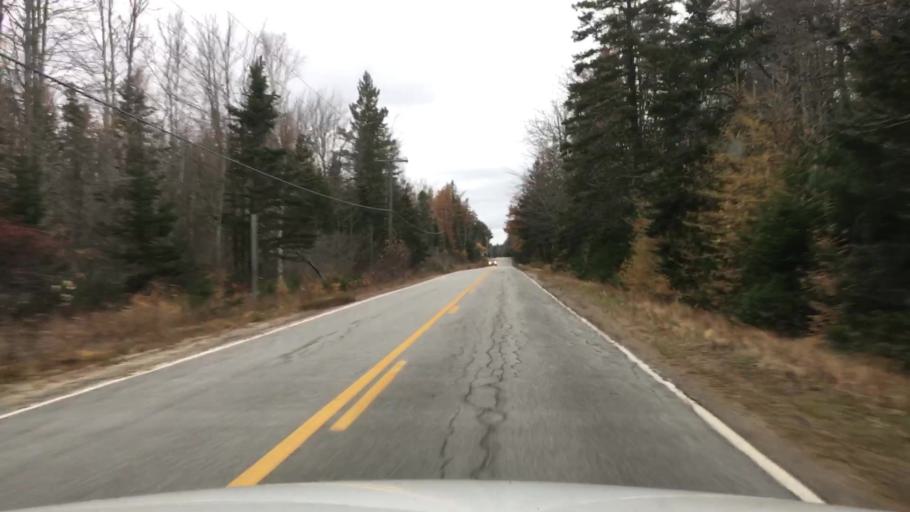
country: US
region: Maine
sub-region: Hancock County
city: Sedgwick
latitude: 44.2792
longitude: -68.5537
